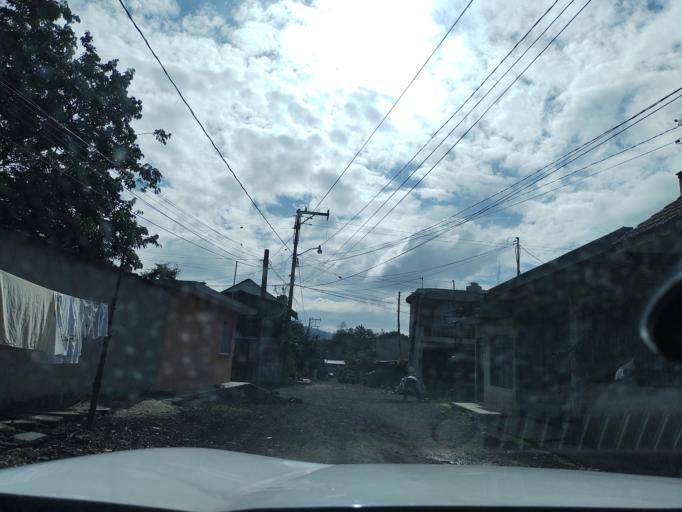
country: MX
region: Veracruz
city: Coatepec
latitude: 19.4811
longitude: -96.9331
